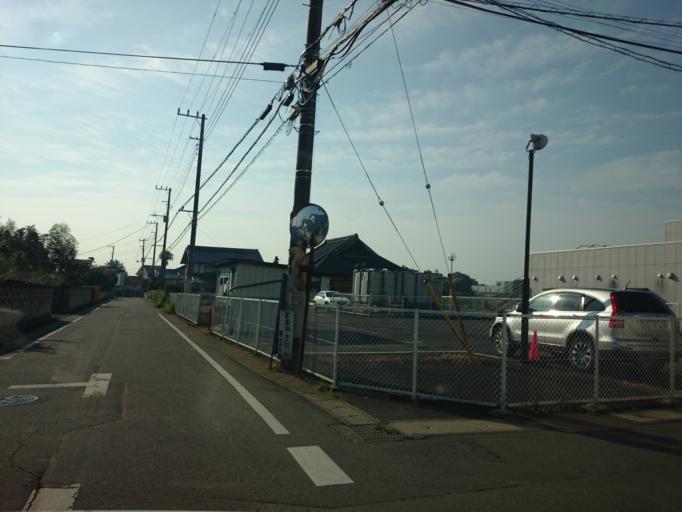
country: JP
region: Ibaraki
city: Tsukuba
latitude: 36.1092
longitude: 140.0816
